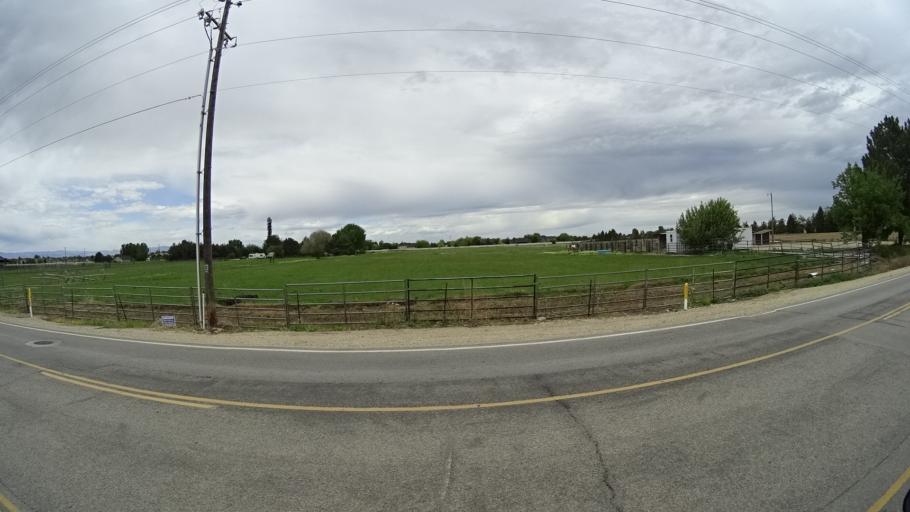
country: US
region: Idaho
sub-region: Ada County
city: Kuna
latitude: 43.5196
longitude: -116.4137
